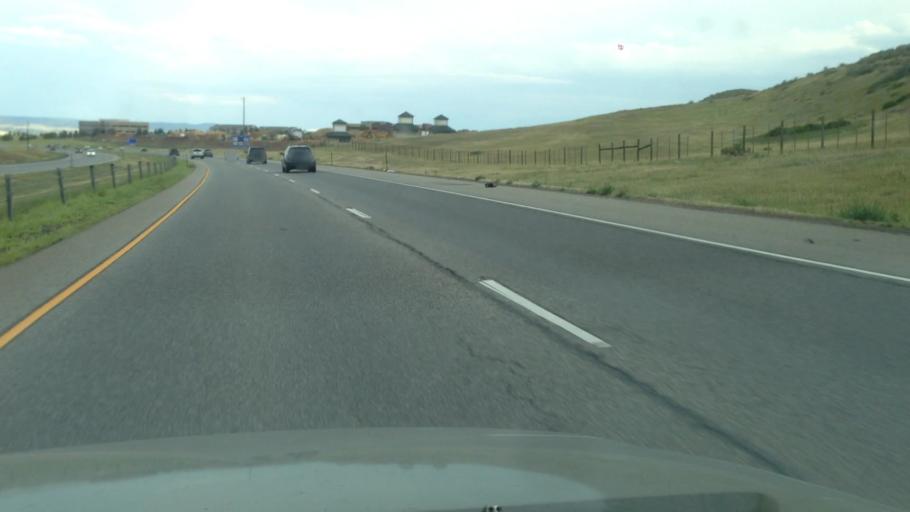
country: US
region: Colorado
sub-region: Jefferson County
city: Ken Caryl
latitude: 39.5640
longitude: -105.1275
